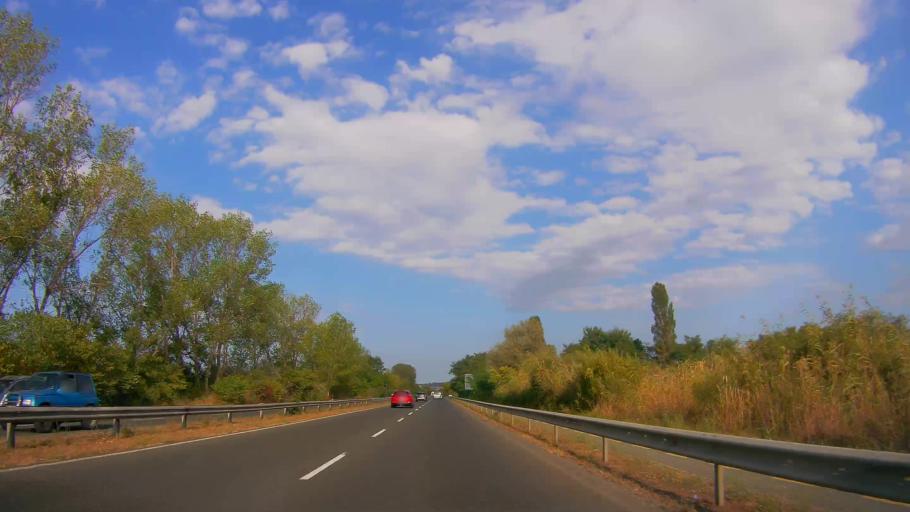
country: BG
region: Burgas
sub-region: Obshtina Burgas
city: Burgas
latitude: 42.4523
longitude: 27.4477
